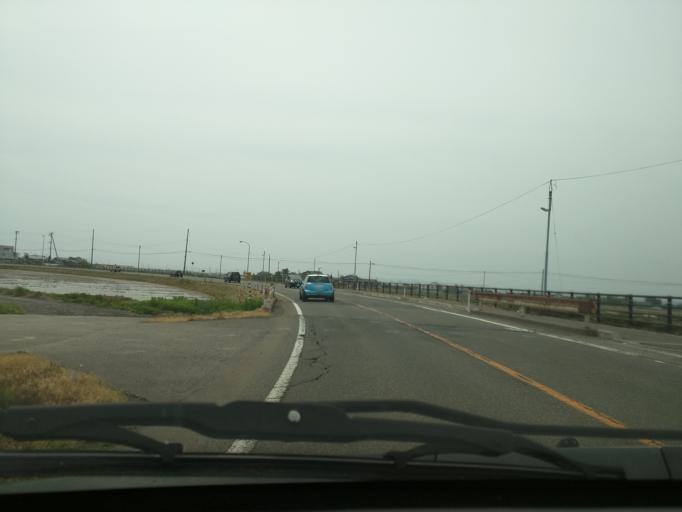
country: JP
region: Niigata
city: Mitsuke
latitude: 37.5547
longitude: 138.9231
